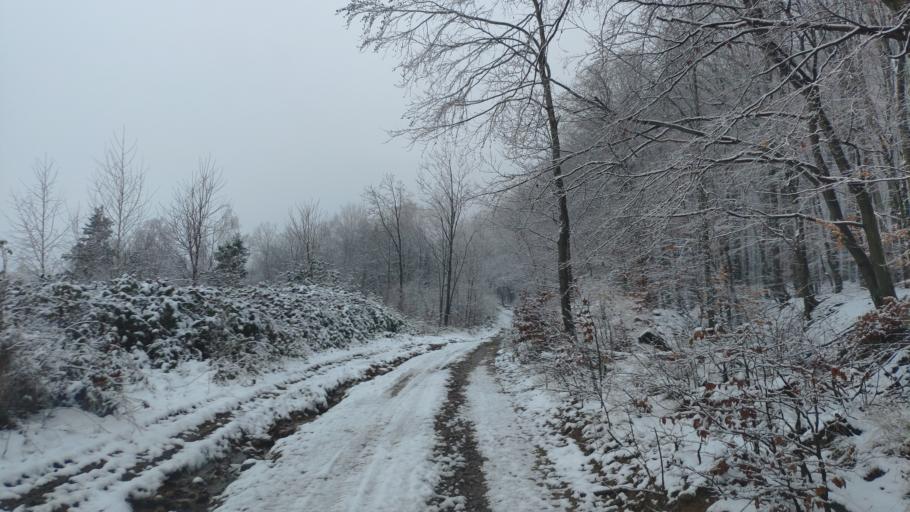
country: SK
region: Kosicky
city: Moldava nad Bodvou
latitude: 48.7430
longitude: 21.0829
